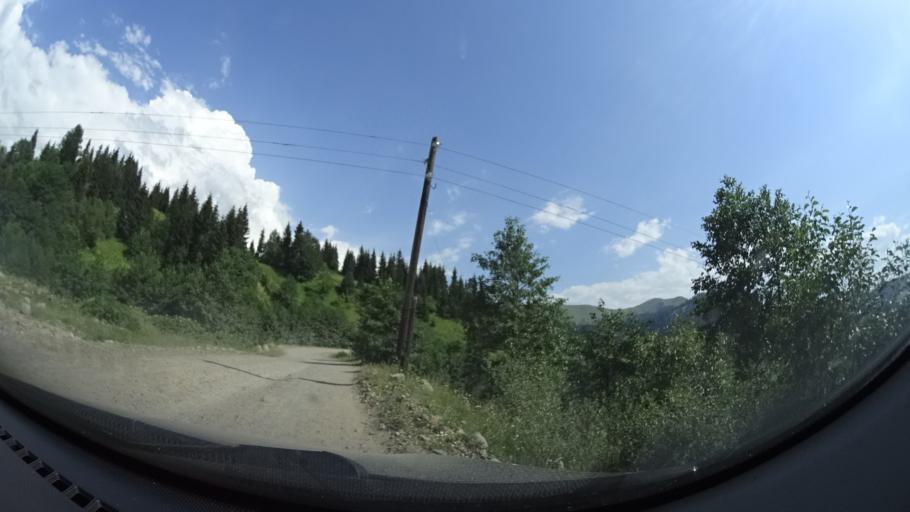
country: GE
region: Ajaria
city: Dioknisi
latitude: 41.6424
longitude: 42.4928
